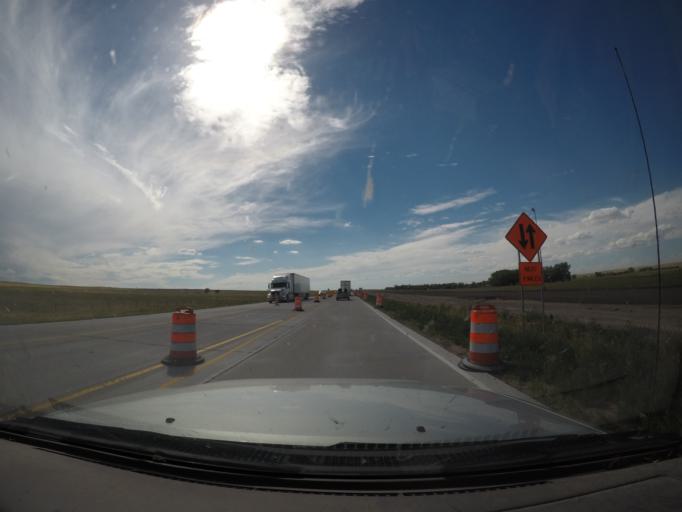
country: US
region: Nebraska
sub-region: Deuel County
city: Chappell
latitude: 41.0842
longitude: -102.4859
